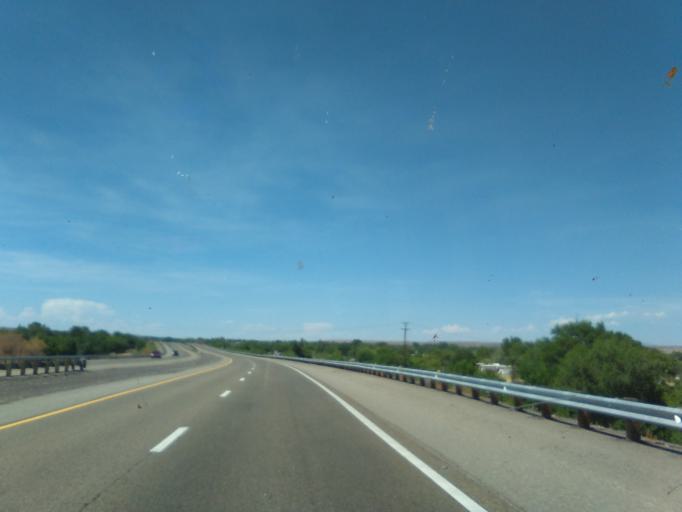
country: US
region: New Mexico
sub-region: Socorro County
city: Socorro
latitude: 34.0532
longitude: -106.8871
